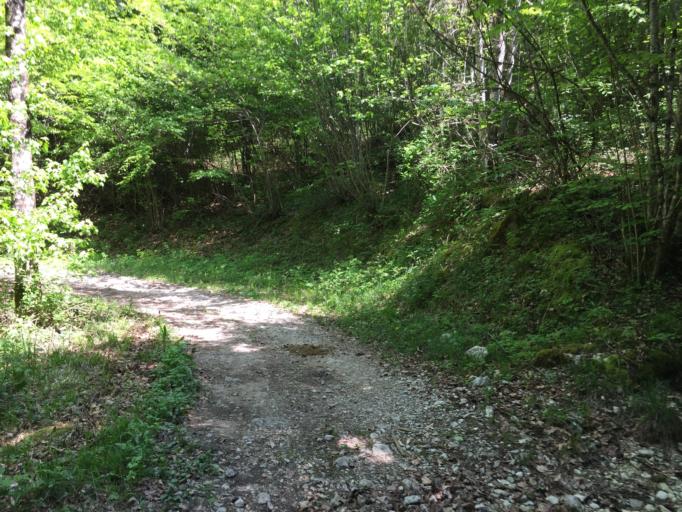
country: FR
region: Rhone-Alpes
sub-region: Departement de la Savoie
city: Mery
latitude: 45.6617
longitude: 5.9506
